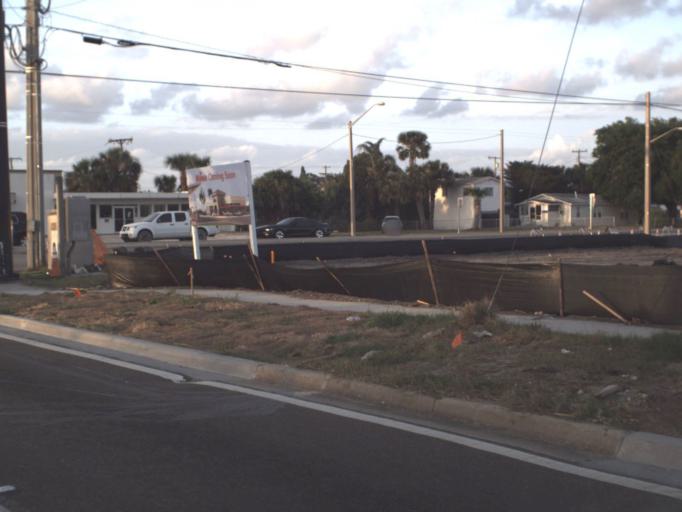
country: US
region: Florida
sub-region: Brevard County
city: Rockledge
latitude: 28.3553
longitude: -80.7425
